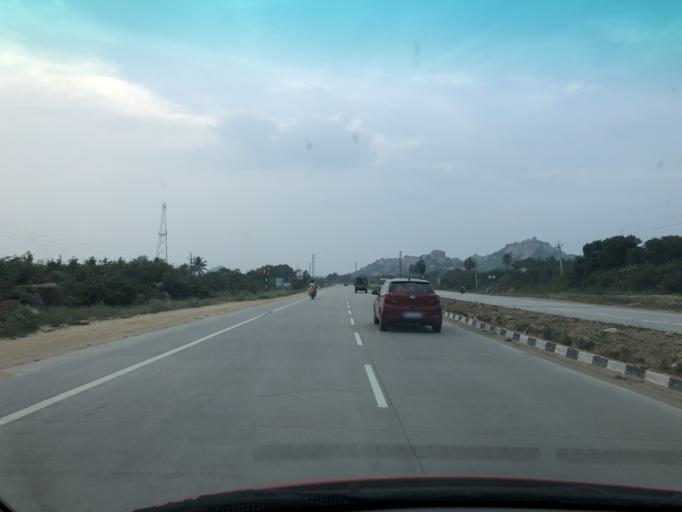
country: IN
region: Andhra Pradesh
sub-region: Chittoor
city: Chittoor
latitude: 13.1961
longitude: 79.0028
